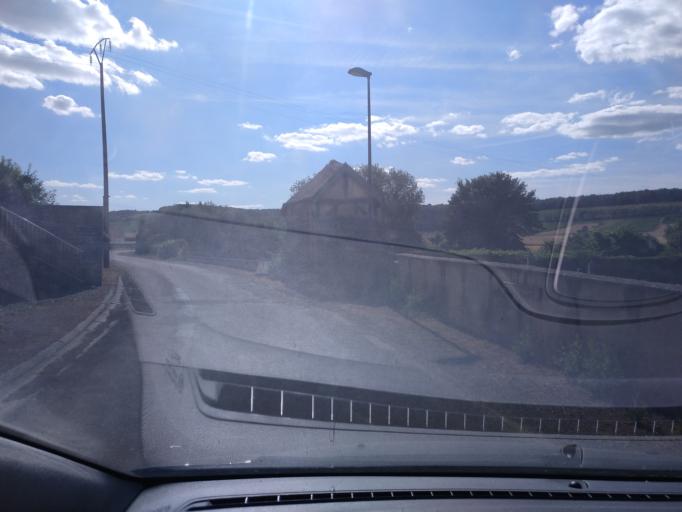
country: FR
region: Bourgogne
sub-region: Departement de la Cote-d'Or
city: Chatillon-sur-Seine
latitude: 47.9433
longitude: 4.6512
